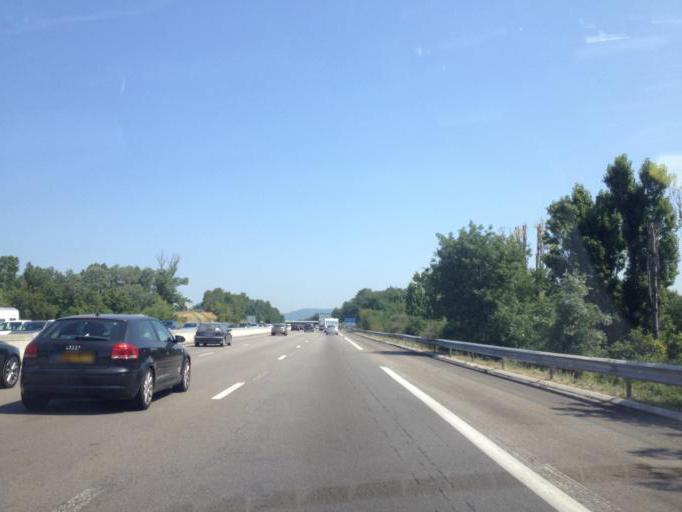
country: FR
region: Rhone-Alpes
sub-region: Departement de la Drome
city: Montboucher-sur-Jabron
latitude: 44.5462
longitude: 4.8085
